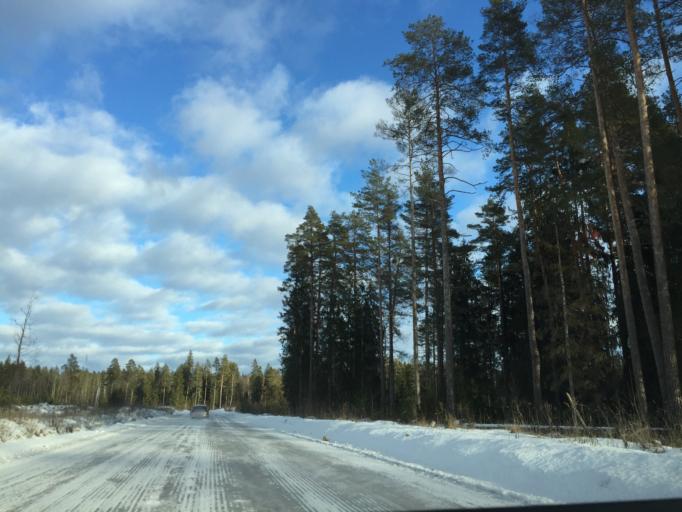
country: LV
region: Ogre
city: Jumprava
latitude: 56.5913
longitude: 24.9788
